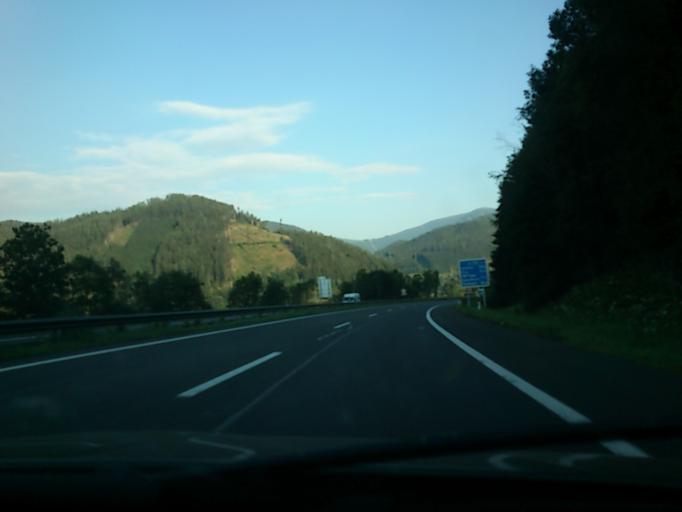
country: AT
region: Styria
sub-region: Politischer Bezirk Leoben
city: Sankt Michael in Obersteiermark
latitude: 47.3322
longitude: 15.0218
